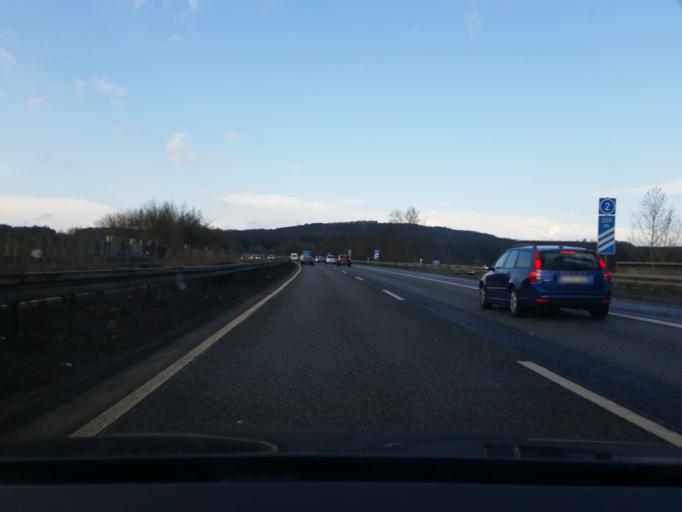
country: DE
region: Hesse
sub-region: Regierungsbezirk Giessen
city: Alten Buseck
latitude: 50.6046
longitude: 8.7169
